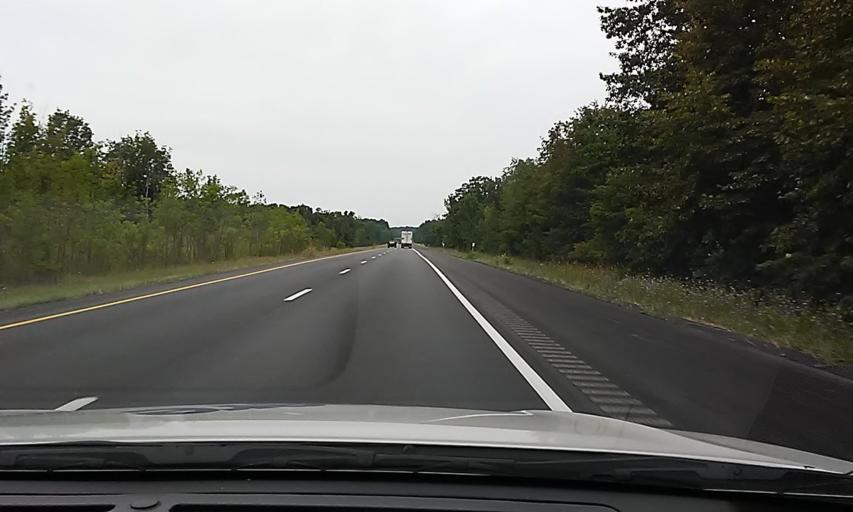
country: US
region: New York
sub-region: Genesee County
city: Bergen
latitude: 43.0572
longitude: -77.9440
